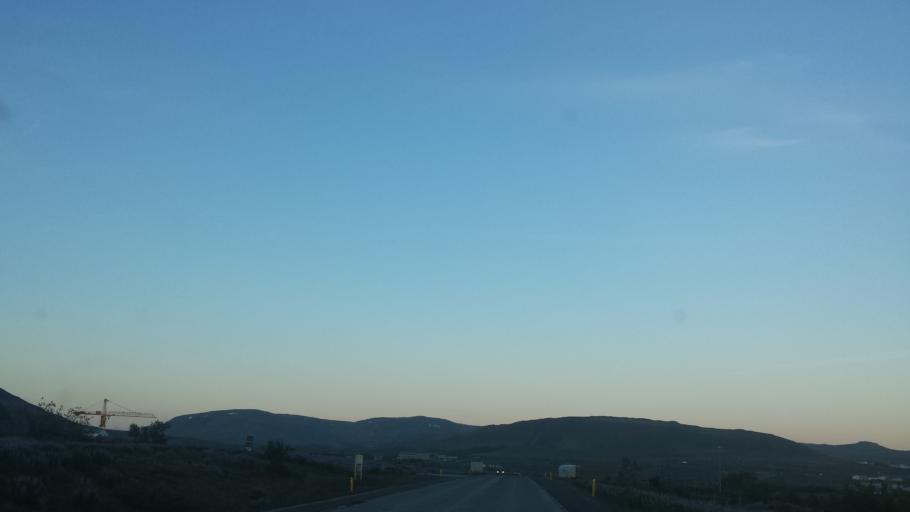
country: IS
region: Capital Region
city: Mosfellsbaer
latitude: 64.1950
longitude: -21.6996
